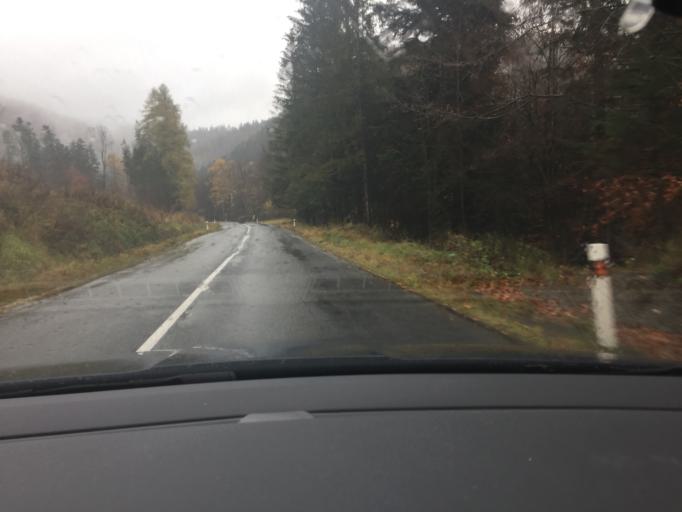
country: SK
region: Presovsky
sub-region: Okres Poprad
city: Zdiar
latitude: 49.2450
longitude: 20.3096
